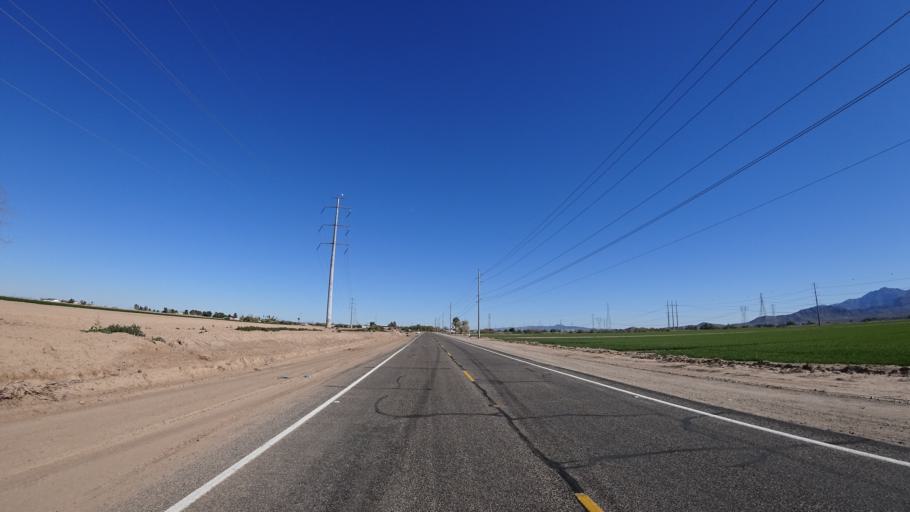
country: US
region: Arizona
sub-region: Maricopa County
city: Goodyear
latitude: 33.4064
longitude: -112.3630
